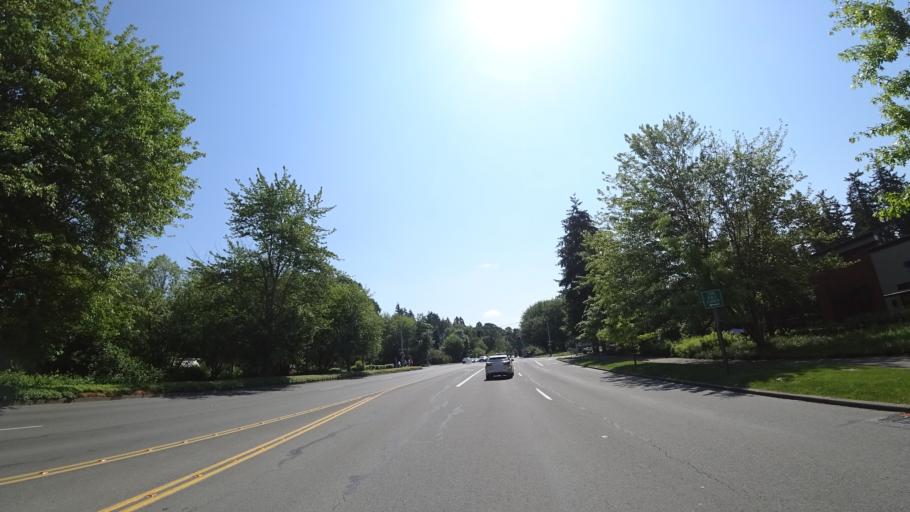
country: US
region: Oregon
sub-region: Washington County
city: Durham
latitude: 45.4187
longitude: -122.7253
